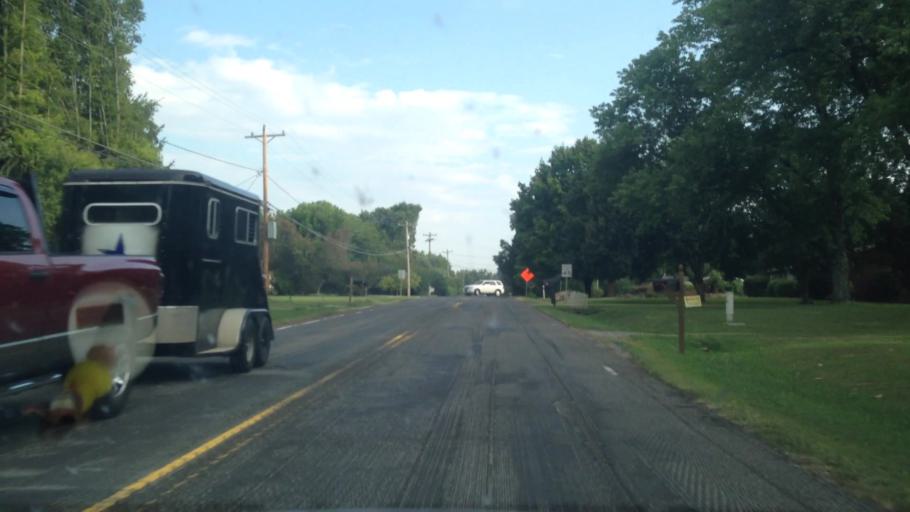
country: US
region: North Carolina
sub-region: Forsyth County
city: Kernersville
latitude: 36.0574
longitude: -80.0657
